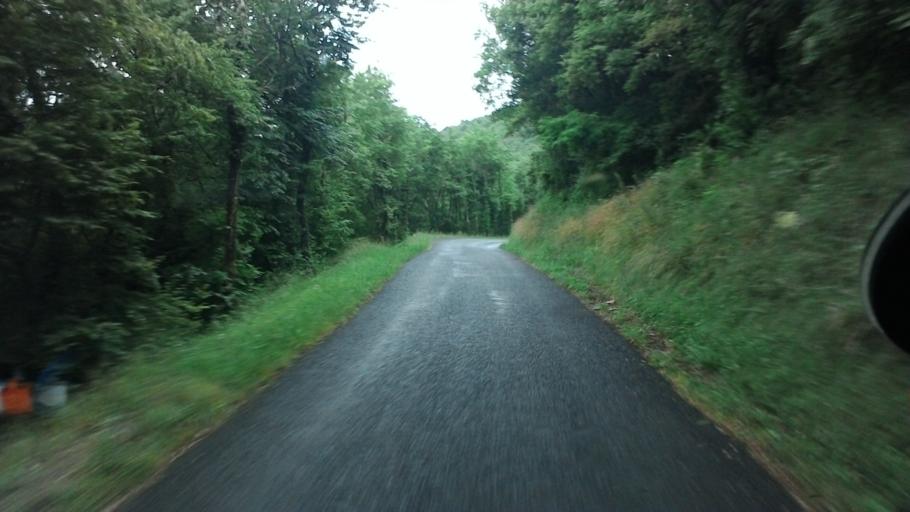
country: FR
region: Rhone-Alpes
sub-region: Departement de l'Ain
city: Belley
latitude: 45.7531
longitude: 5.5967
